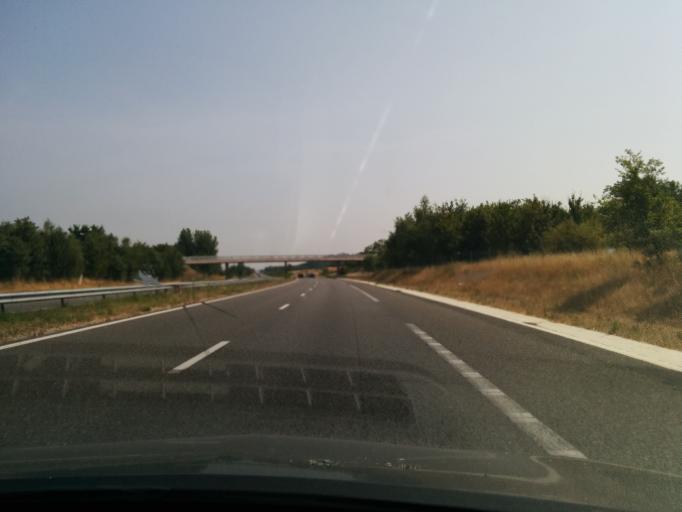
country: FR
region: Midi-Pyrenees
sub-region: Departement du Tarn
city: Lisle-sur-Tarn
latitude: 43.8169
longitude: 1.8099
